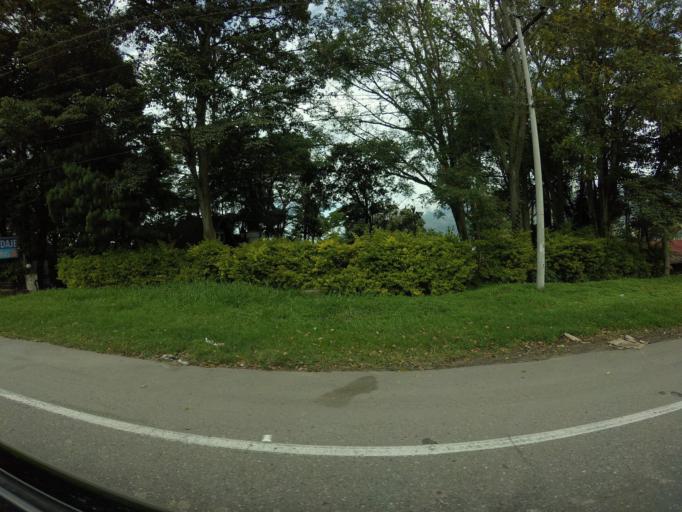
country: CO
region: Cundinamarca
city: Silvania
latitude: 4.3722
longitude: -74.3864
